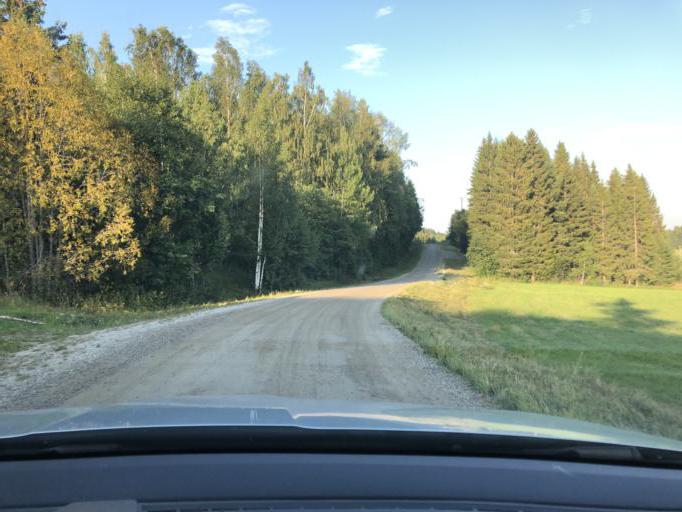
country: SE
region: Vaesternorrland
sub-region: Kramfors Kommun
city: Bollstabruk
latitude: 63.0512
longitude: 17.6942
